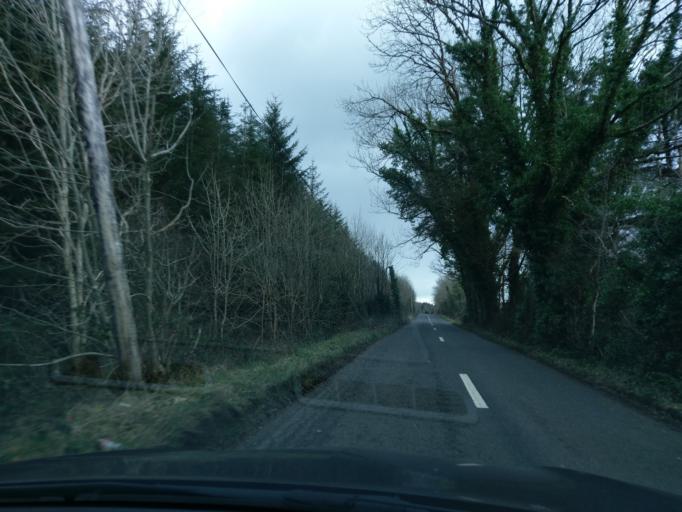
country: IE
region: Connaught
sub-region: County Galway
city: Athenry
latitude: 53.3998
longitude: -8.6292
